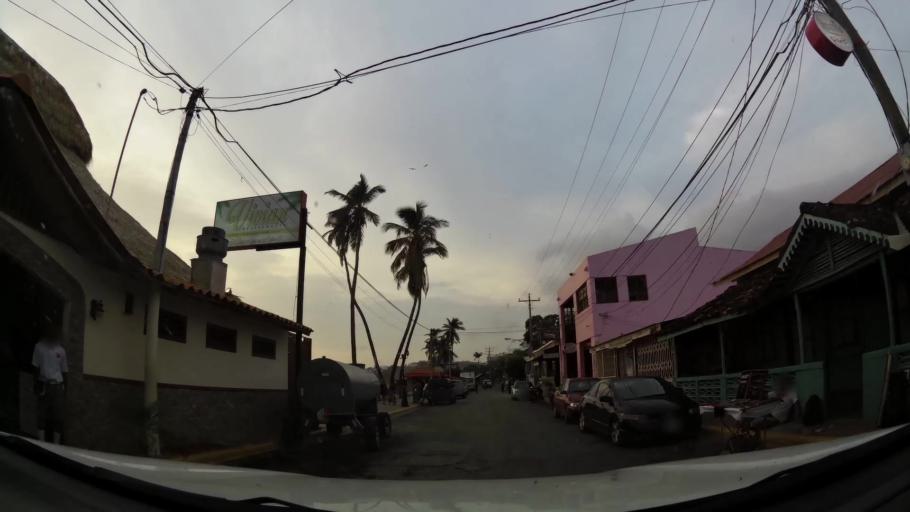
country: NI
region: Rivas
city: San Juan del Sur
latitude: 11.2545
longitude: -85.8725
